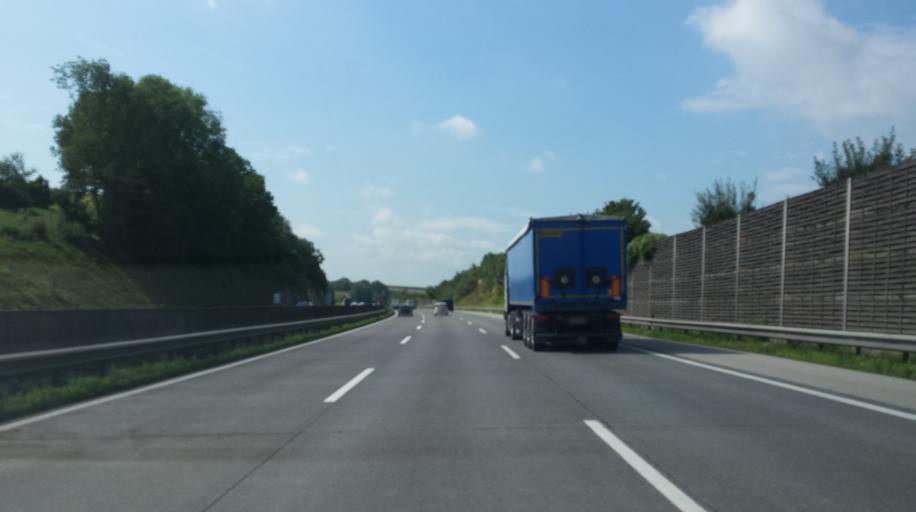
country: AT
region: Lower Austria
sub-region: Politischer Bezirk Melk
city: Erlauf
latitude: 48.1826
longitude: 15.1886
